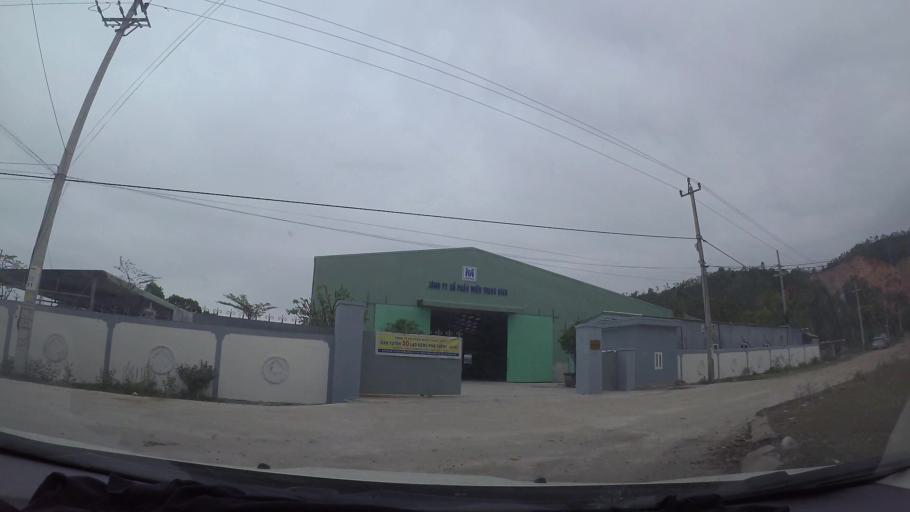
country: VN
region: Da Nang
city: Lien Chieu
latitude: 16.0687
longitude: 108.1413
